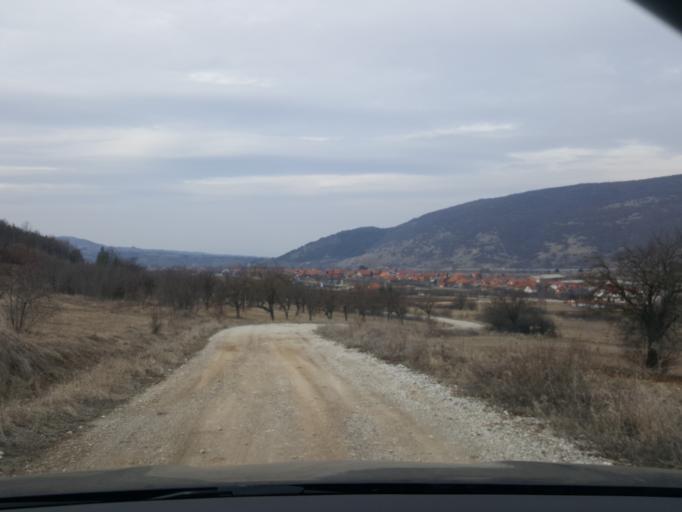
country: RS
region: Central Serbia
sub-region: Pirotski Okrug
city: Dimitrovgrad
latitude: 43.0070
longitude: 22.7487
